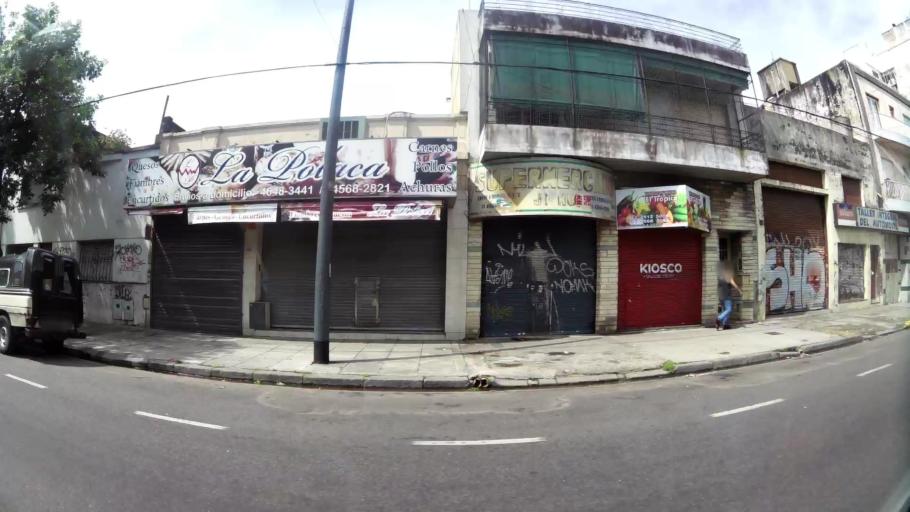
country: AR
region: Buenos Aires F.D.
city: Villa Santa Rita
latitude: -34.6280
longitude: -58.5068
